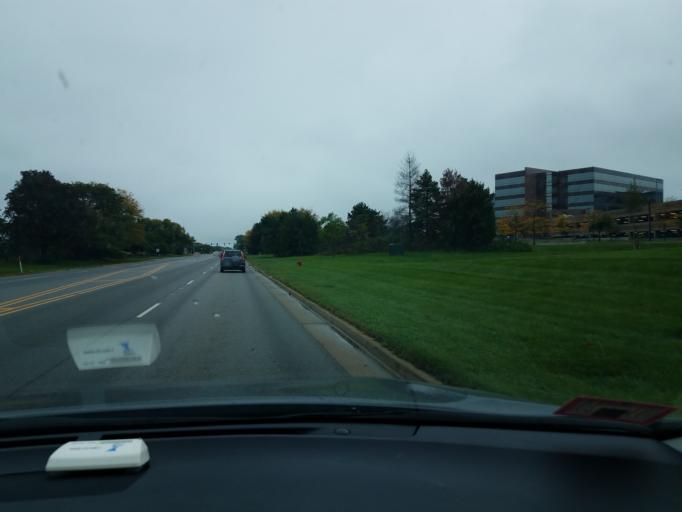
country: US
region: Illinois
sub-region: Lake County
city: Lincolnshire
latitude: 42.1916
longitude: -87.9297
